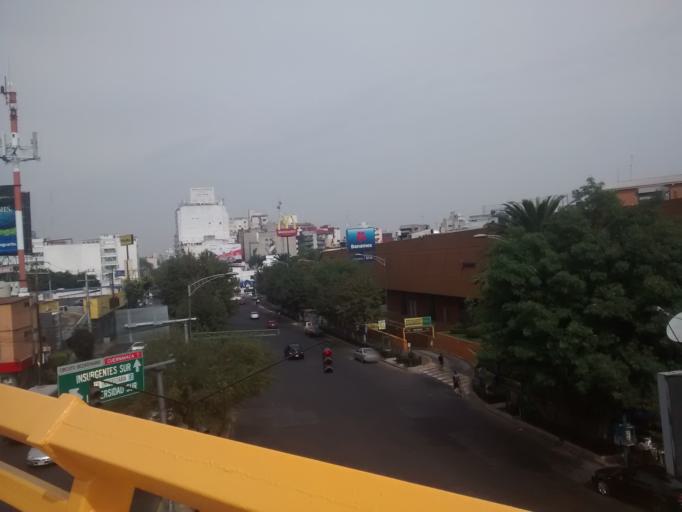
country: MX
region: Mexico City
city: Coyoacan
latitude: 19.3589
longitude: -99.1702
